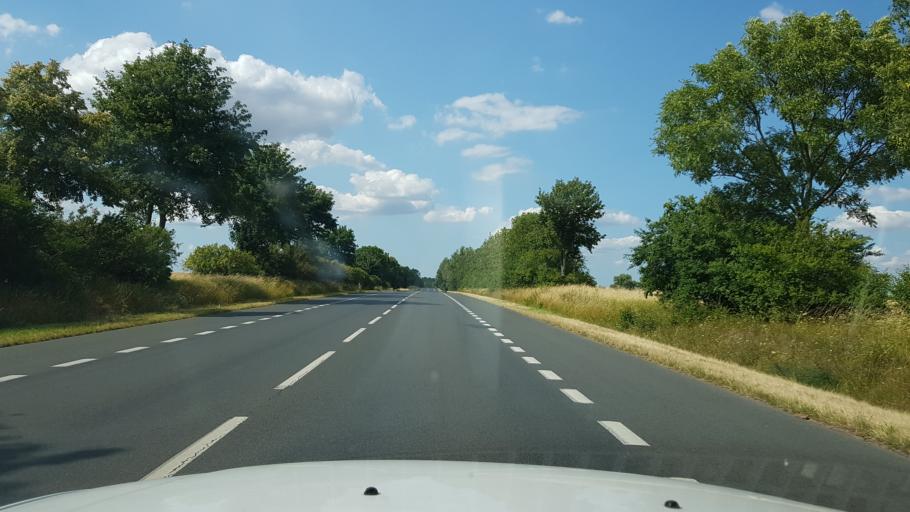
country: PL
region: West Pomeranian Voivodeship
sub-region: Powiat pyrzycki
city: Pyrzyce
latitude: 53.1159
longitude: 14.8933
